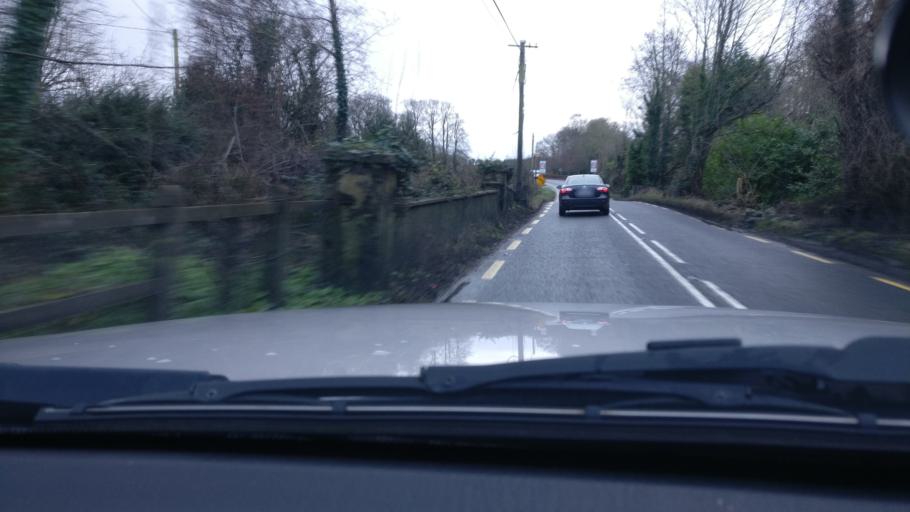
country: IE
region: Leinster
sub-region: An Iarmhi
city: Athlone
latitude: 53.4518
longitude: -7.8846
